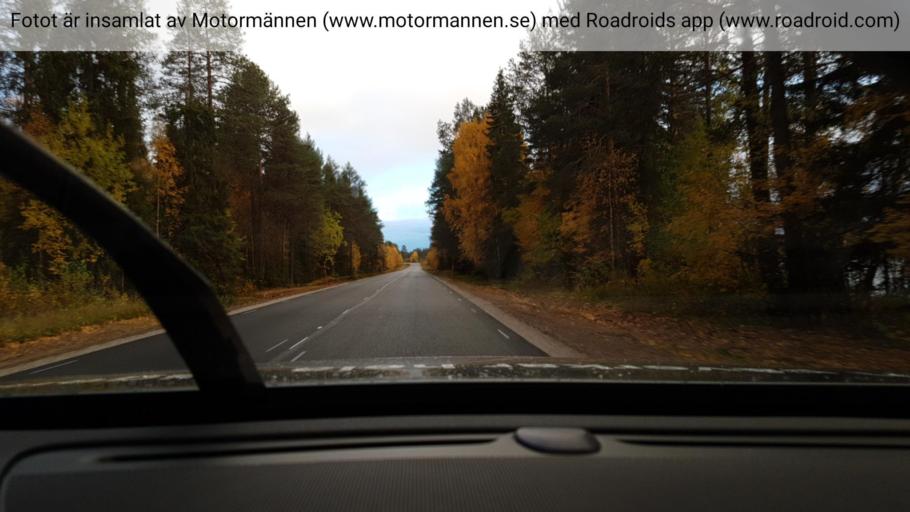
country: SE
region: Norrbotten
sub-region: Overkalix Kommun
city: OEverkalix
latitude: 66.4116
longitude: 22.8052
